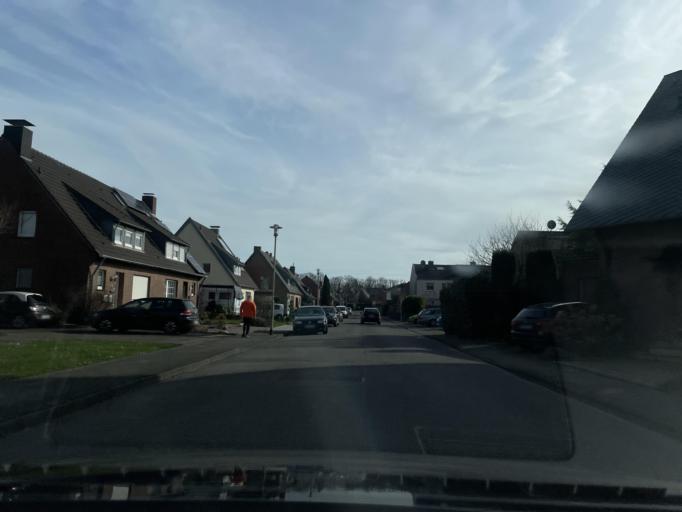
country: DE
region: North Rhine-Westphalia
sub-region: Regierungsbezirk Dusseldorf
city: Monchengladbach
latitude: 51.2267
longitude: 6.4578
